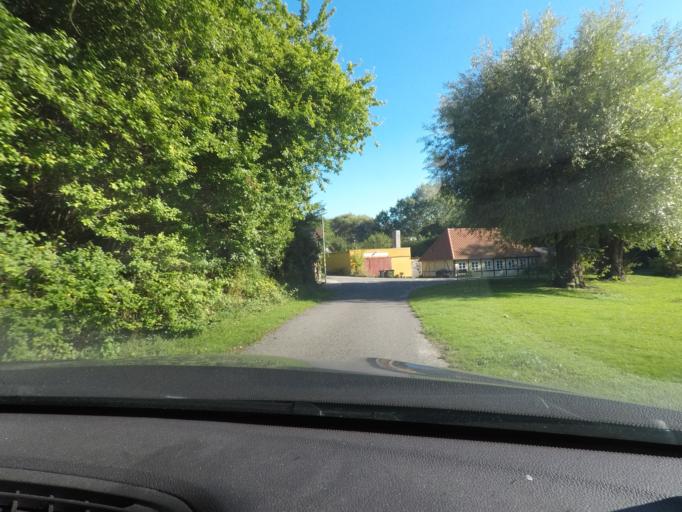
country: DK
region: Zealand
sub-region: Guldborgsund Kommune
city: Sakskobing
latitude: 54.9806
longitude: 11.5316
